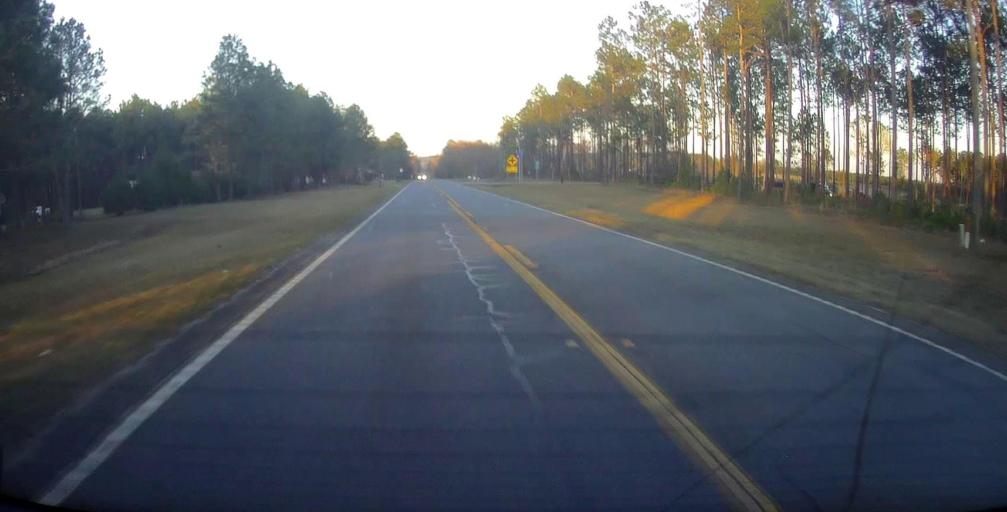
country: US
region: Georgia
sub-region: Dodge County
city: Eastman
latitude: 32.2811
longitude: -83.1070
